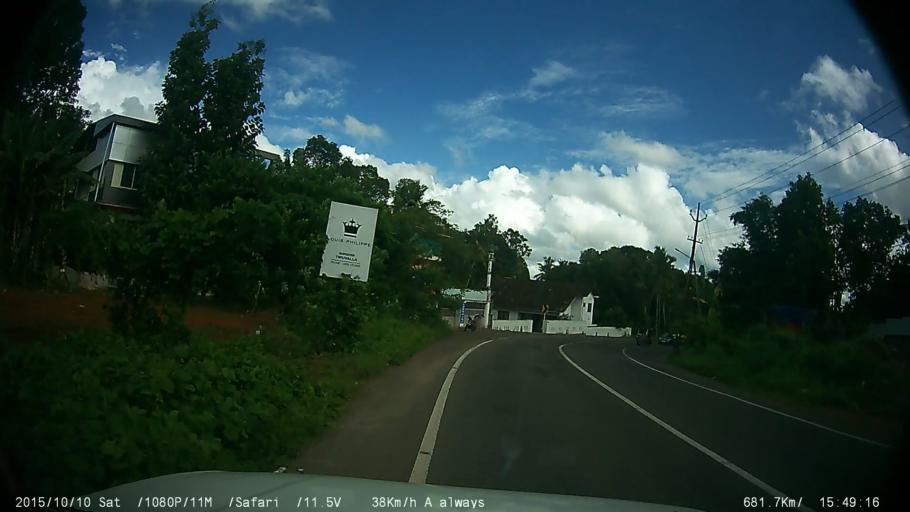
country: IN
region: Kerala
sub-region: Kottayam
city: Changanacheri
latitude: 9.4429
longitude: 76.5511
